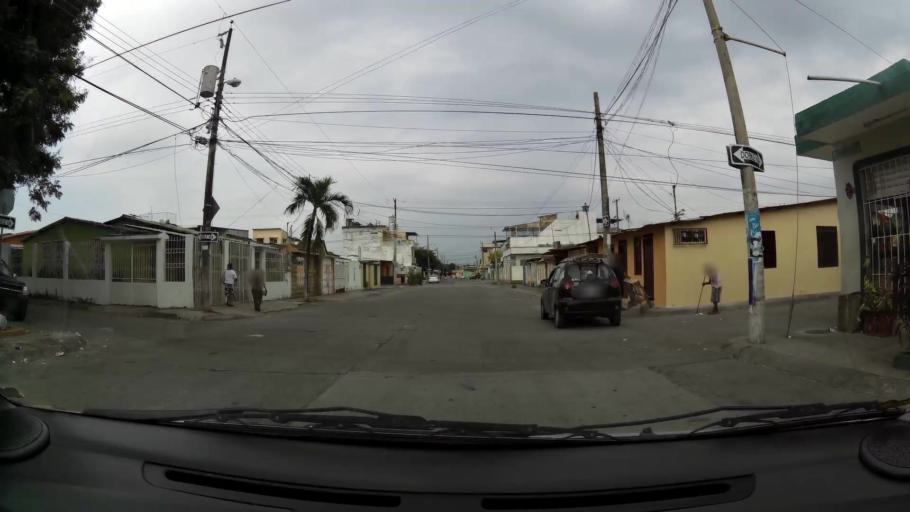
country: EC
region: Guayas
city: Eloy Alfaro
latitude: -2.1176
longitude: -79.8880
